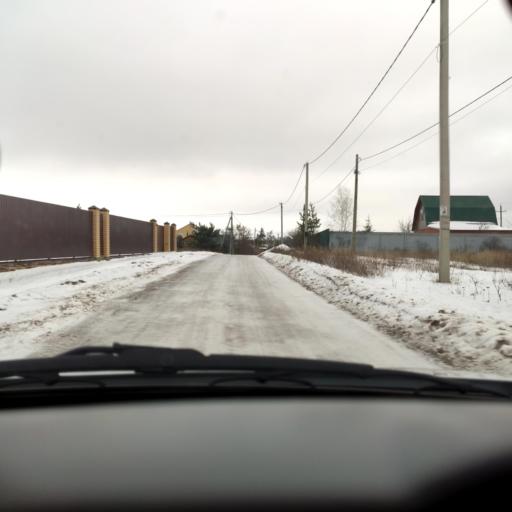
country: RU
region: Voronezj
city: Ramon'
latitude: 51.8849
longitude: 39.2619
